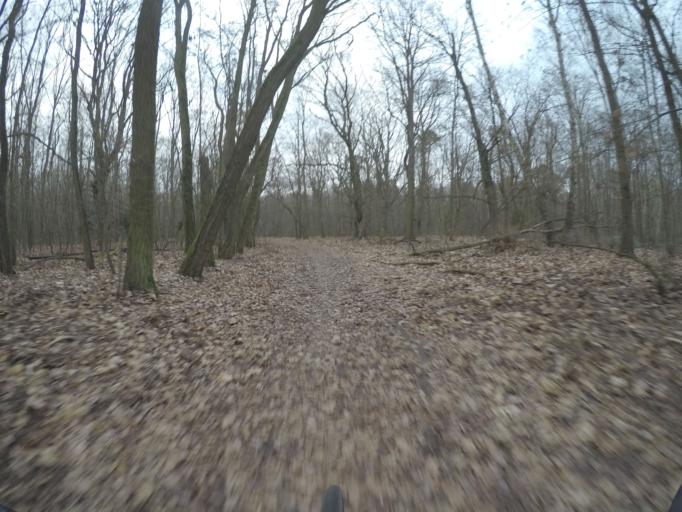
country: DE
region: Berlin
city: Grunau
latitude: 52.4153
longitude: 13.5976
